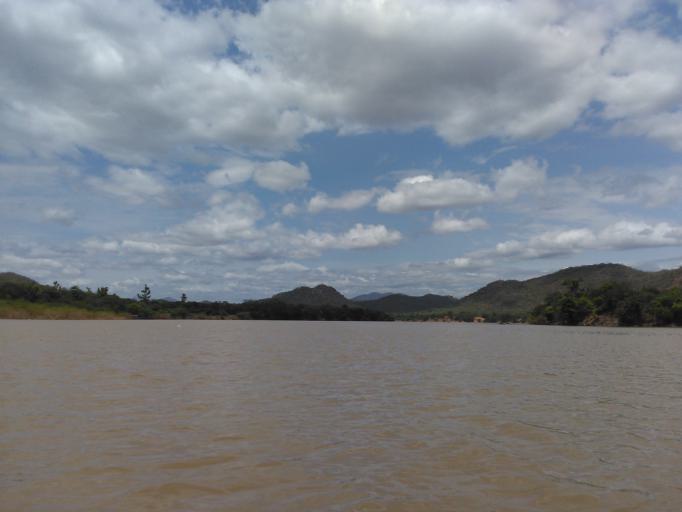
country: IN
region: Tamil Nadu
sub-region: Dharmapuri
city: Pennagaram
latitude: 12.1105
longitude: 77.7751
